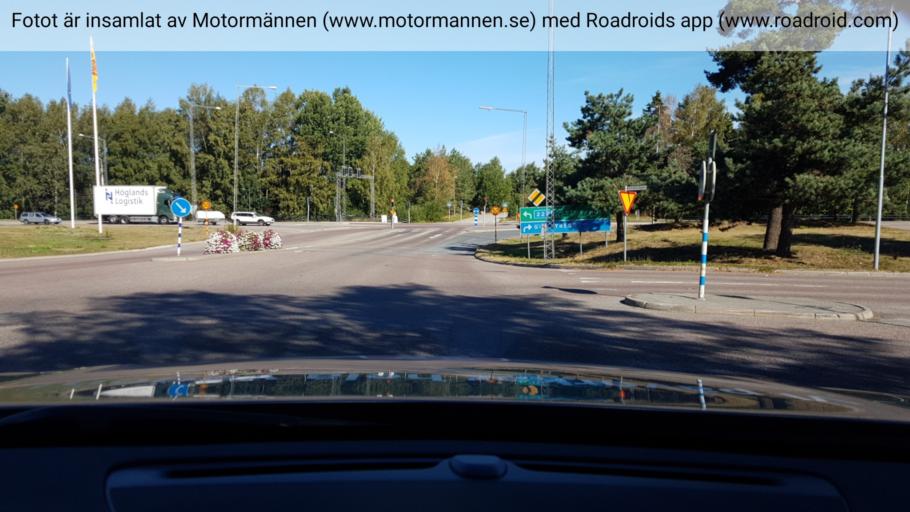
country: SE
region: Stockholm
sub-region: Tyreso Kommun
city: Bollmora
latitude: 59.2487
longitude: 18.2306
